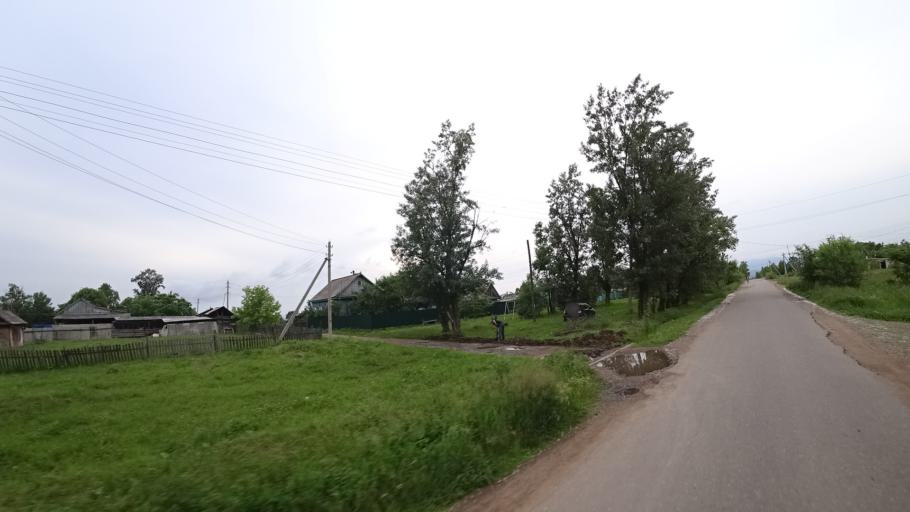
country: RU
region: Primorskiy
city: Novosysoyevka
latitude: 44.2310
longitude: 133.3605
